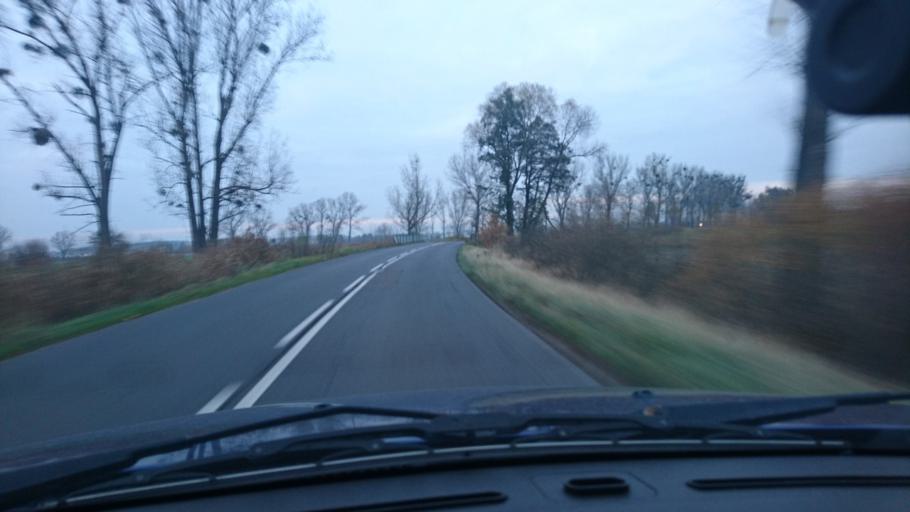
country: PL
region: Greater Poland Voivodeship
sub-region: Powiat ostrowski
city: Odolanow
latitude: 51.5632
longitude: 17.6613
